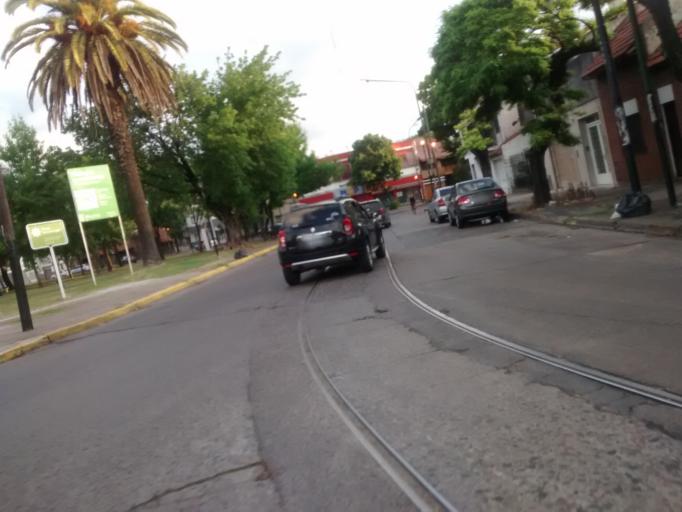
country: AR
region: Buenos Aires
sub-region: Partido de La Plata
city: La Plata
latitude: -34.9214
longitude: -57.9682
